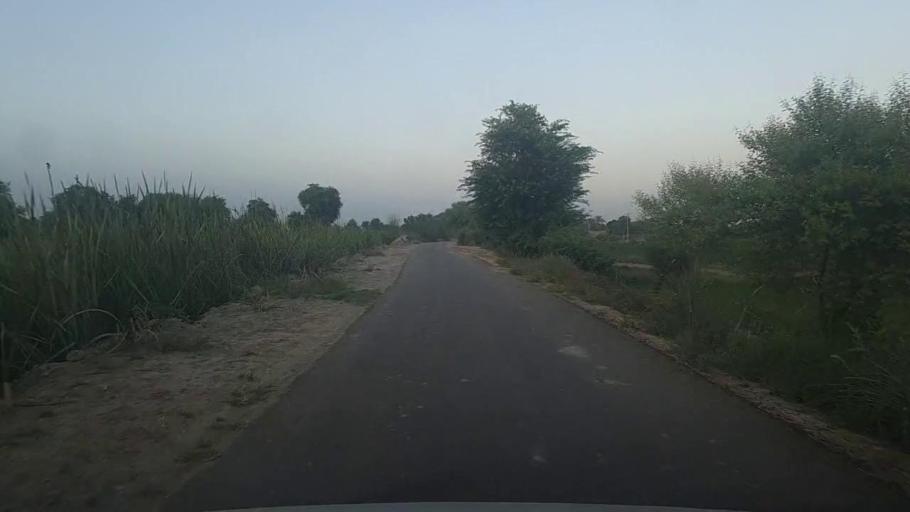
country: PK
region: Sindh
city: Khairpur
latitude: 28.0946
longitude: 69.7353
